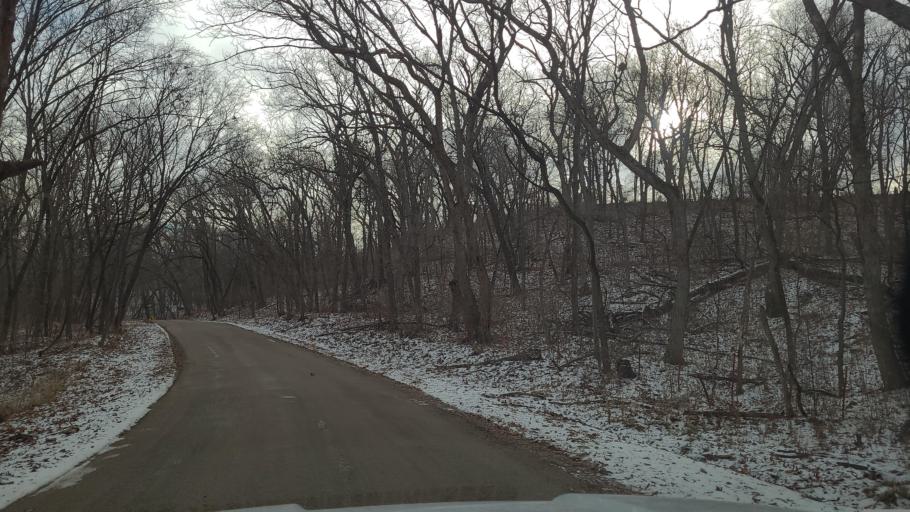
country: US
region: Kansas
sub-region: Shawnee County
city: Topeka
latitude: 39.0510
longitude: -95.5028
